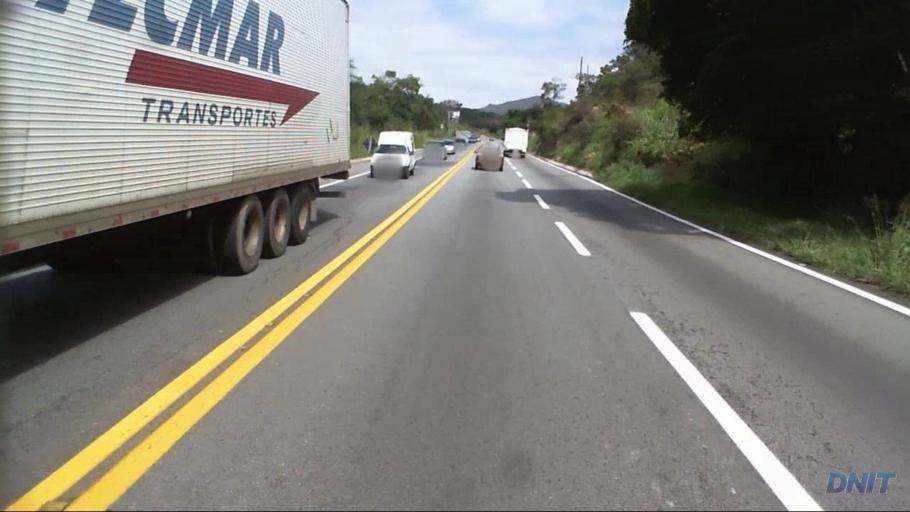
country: BR
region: Minas Gerais
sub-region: Santa Luzia
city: Santa Luzia
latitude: -19.8006
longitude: -43.7619
